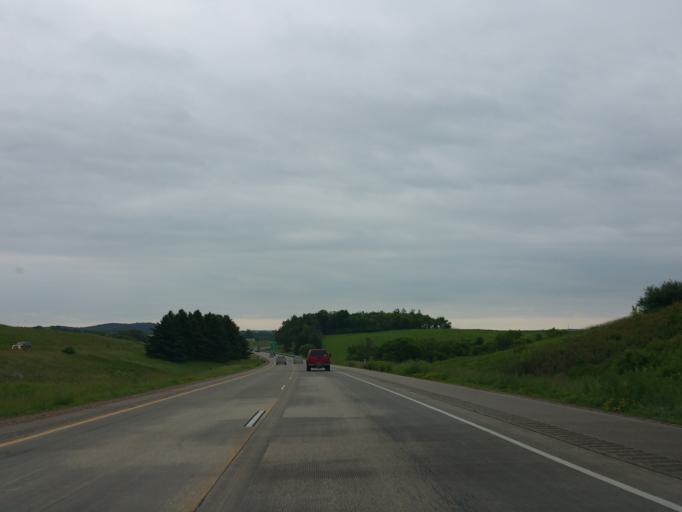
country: US
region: Wisconsin
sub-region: Trempealeau County
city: Osseo
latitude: 44.6028
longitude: -91.2255
